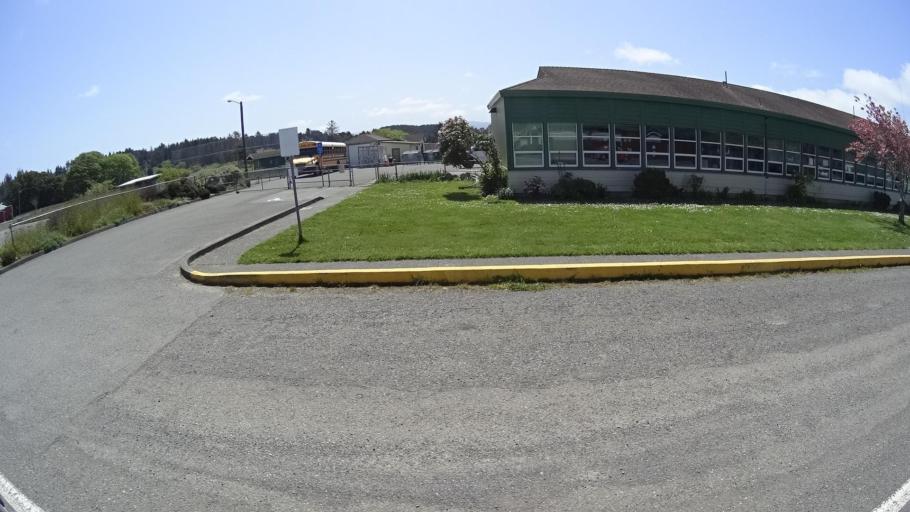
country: US
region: California
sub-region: Humboldt County
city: Fortuna
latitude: 40.6443
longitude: -124.2180
